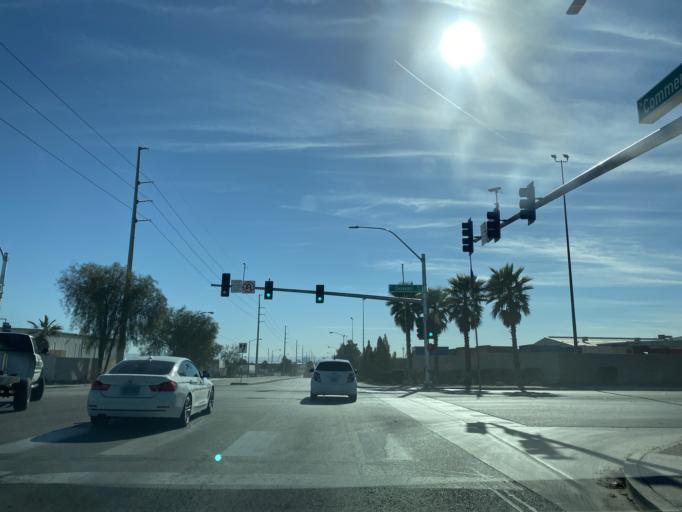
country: US
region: Nevada
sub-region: Clark County
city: North Las Vegas
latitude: 36.2251
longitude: -115.1433
